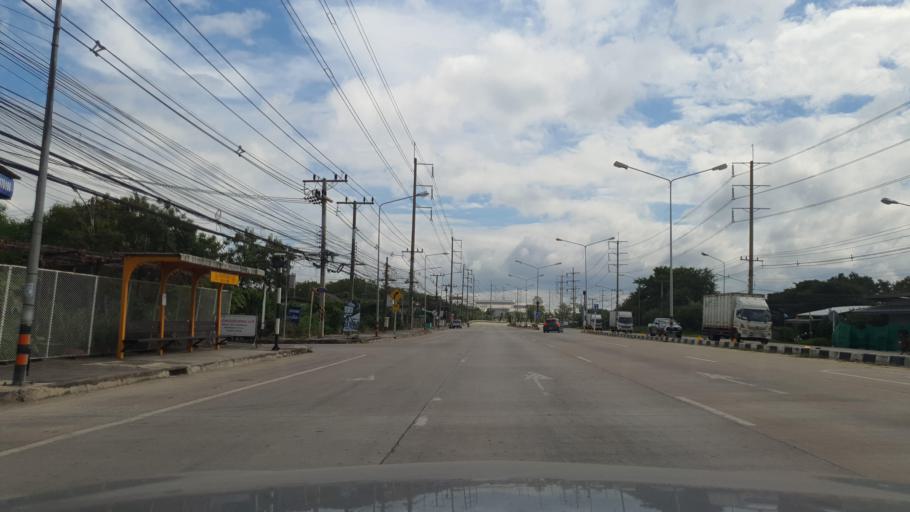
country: TH
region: Chachoengsao
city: Bang Pakong
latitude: 13.5376
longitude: 100.9901
